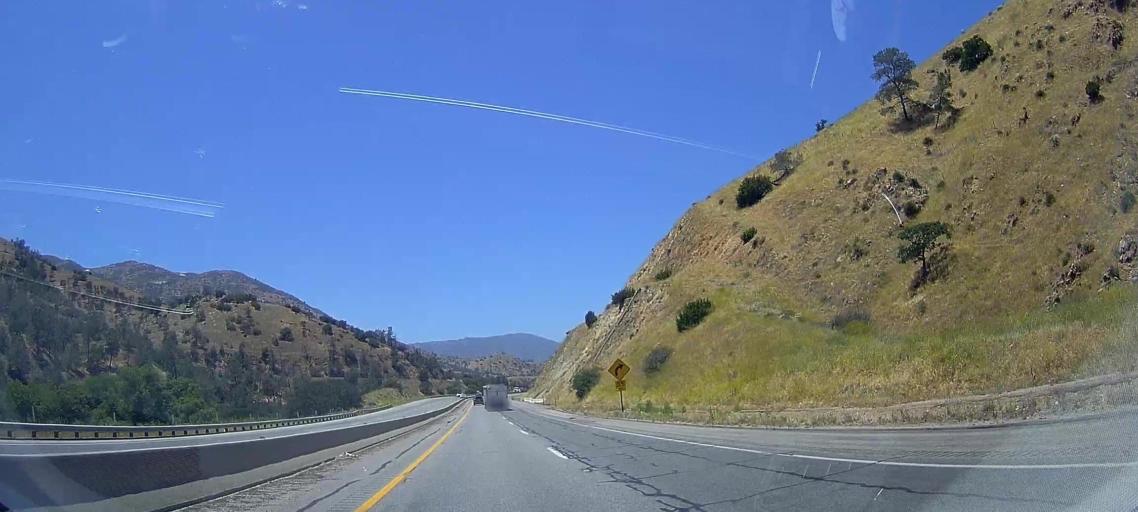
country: US
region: California
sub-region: Kern County
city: Golden Hills
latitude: 35.1818
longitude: -118.4929
